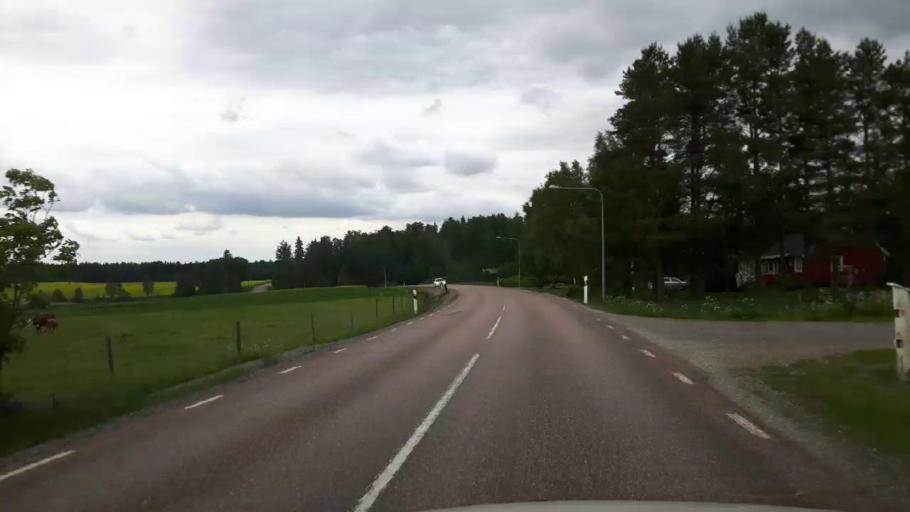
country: SE
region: Vaestmanland
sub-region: Kopings Kommun
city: Kolsva
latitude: 59.7196
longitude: 15.7920
